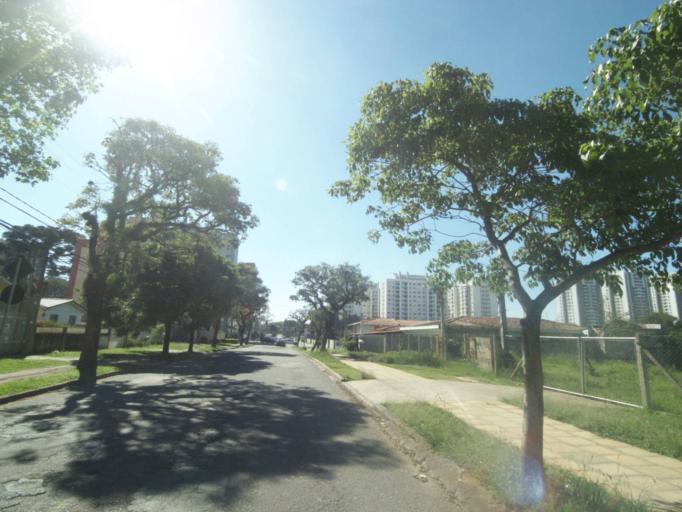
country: BR
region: Parana
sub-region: Curitiba
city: Curitiba
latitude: -25.3912
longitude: -49.2356
